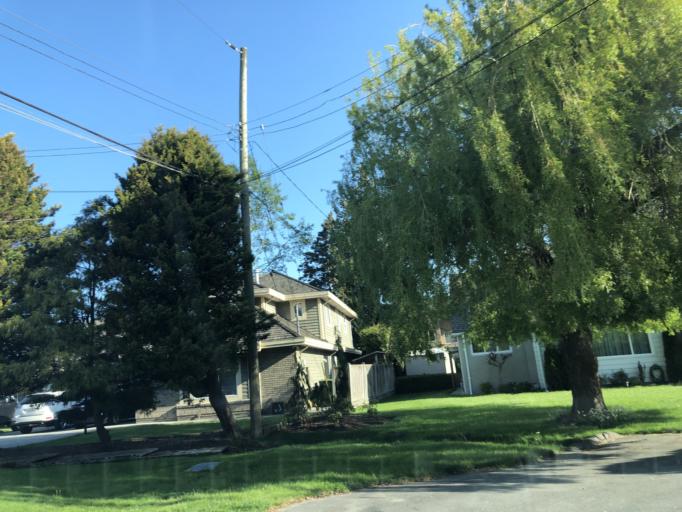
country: CA
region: British Columbia
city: Richmond
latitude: 49.1422
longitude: -123.1169
